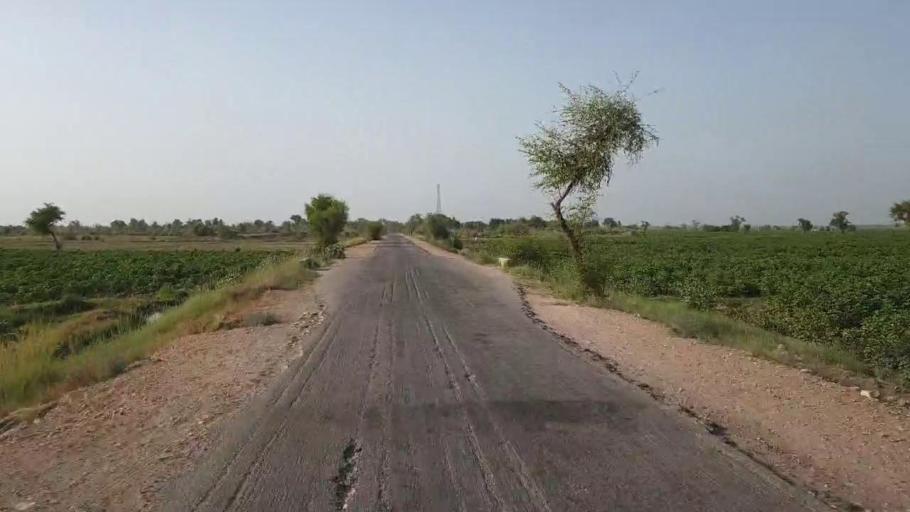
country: PK
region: Sindh
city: Jam Sahib
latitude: 26.4760
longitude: 68.8599
